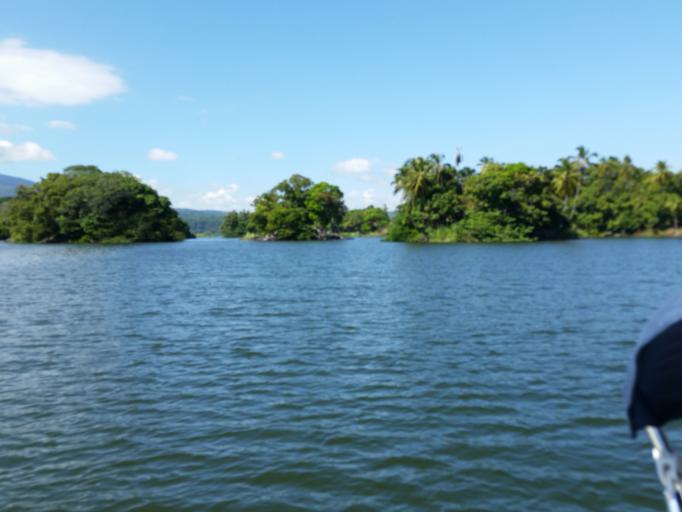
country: NI
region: Granada
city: Granada
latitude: 11.8782
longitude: -85.8954
